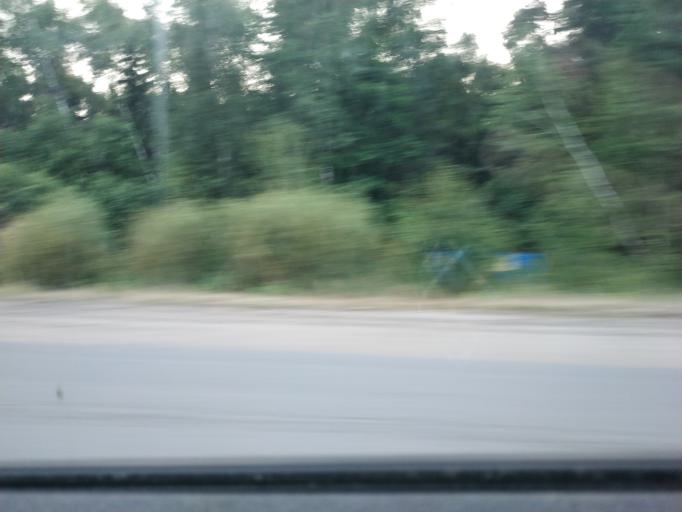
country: RU
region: Moskovskaya
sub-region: Shchelkovskiy Rayon
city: Grebnevo
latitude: 55.9698
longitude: 38.0860
